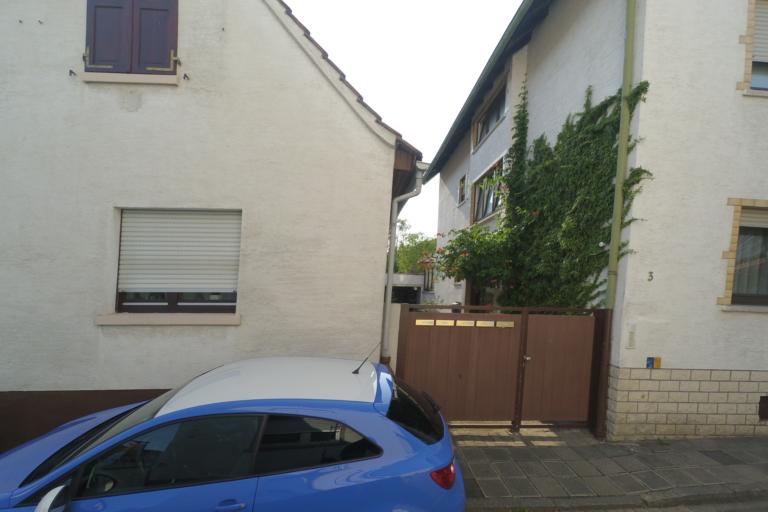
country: DE
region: Hesse
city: Viernheim
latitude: 49.5373
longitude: 8.5861
